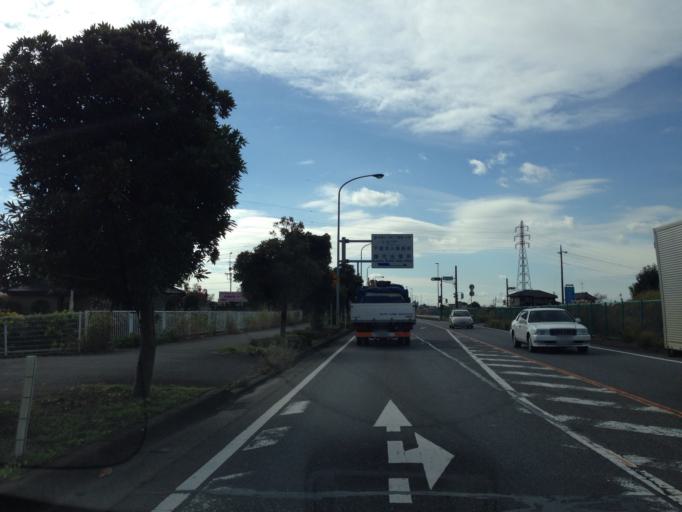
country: JP
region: Ibaraki
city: Fujishiro
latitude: 35.9217
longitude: 140.1035
